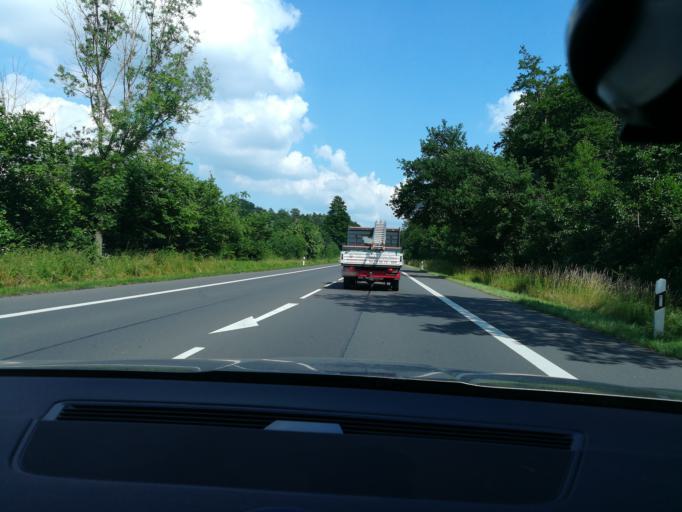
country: DE
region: North Rhine-Westphalia
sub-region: Regierungsbezirk Detmold
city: Petershagen
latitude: 52.3799
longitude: 8.9270
